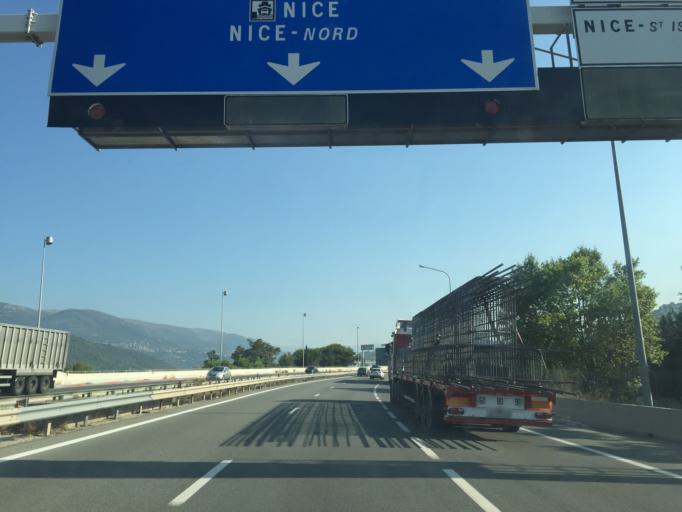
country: FR
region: Provence-Alpes-Cote d'Azur
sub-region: Departement des Alpes-Maritimes
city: Saint-Laurent-du-Var
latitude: 43.7037
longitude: 7.1883
